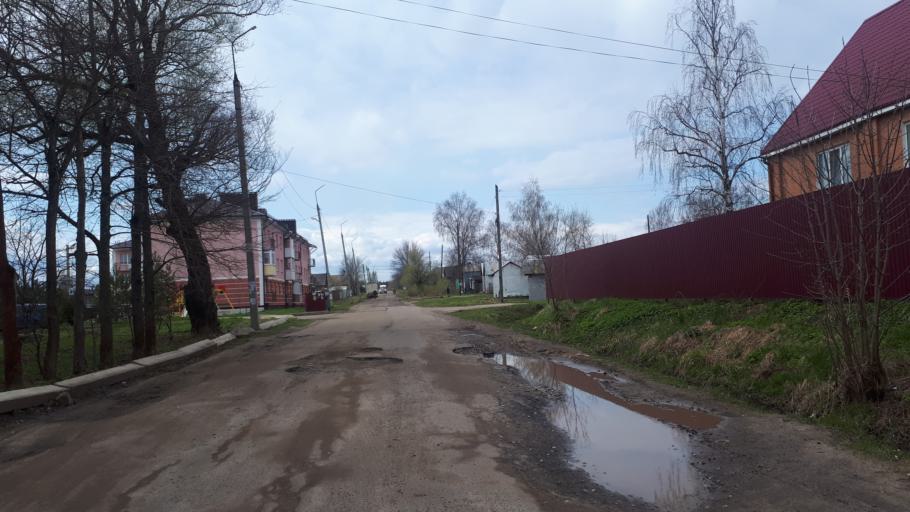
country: RU
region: Jaroslavl
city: Konstantinovskiy
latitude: 57.8285
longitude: 39.5844
